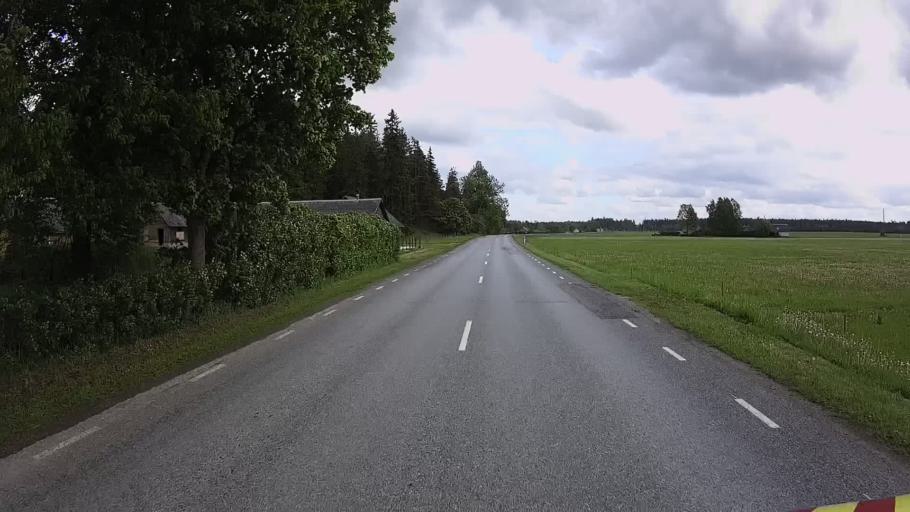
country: EE
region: Laeaene-Virumaa
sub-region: Vinni vald
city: Vinni
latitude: 59.1902
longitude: 26.5720
